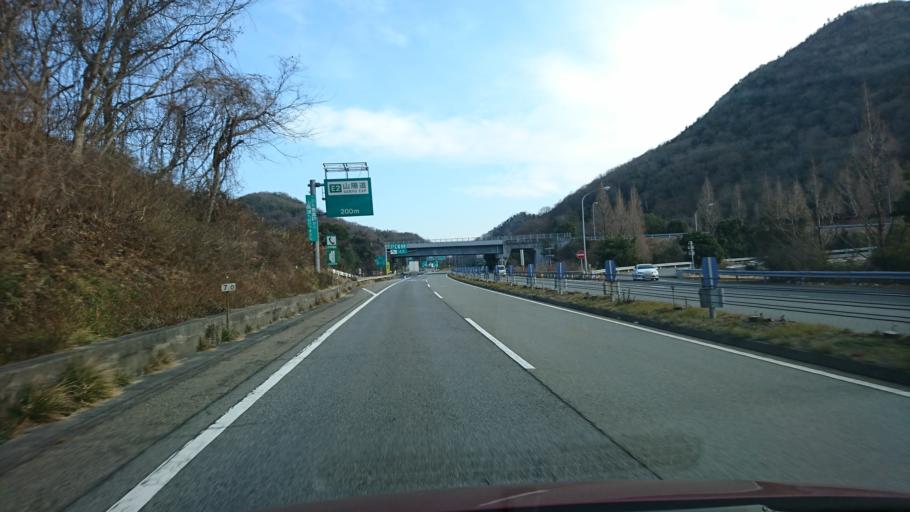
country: JP
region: Hyogo
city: Himeji
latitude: 34.8544
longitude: 134.7354
